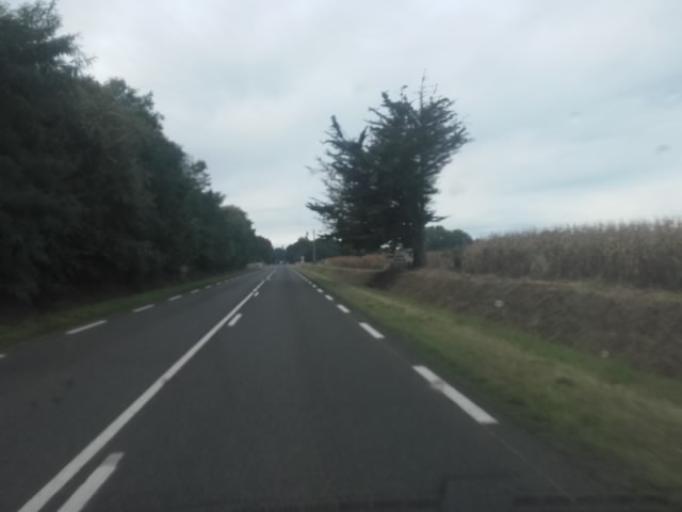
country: FR
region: Brittany
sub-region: Departement des Cotes-d'Armor
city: Plelo
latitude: 48.5767
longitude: -2.9281
